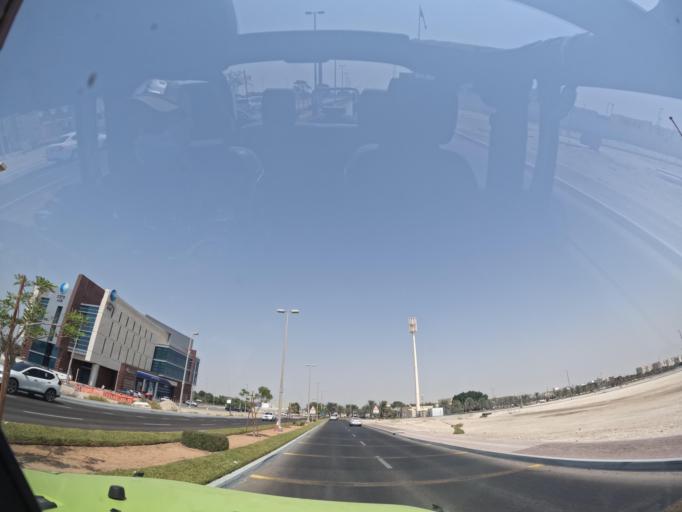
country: AE
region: Abu Dhabi
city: Abu Dhabi
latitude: 24.3178
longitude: 54.6114
